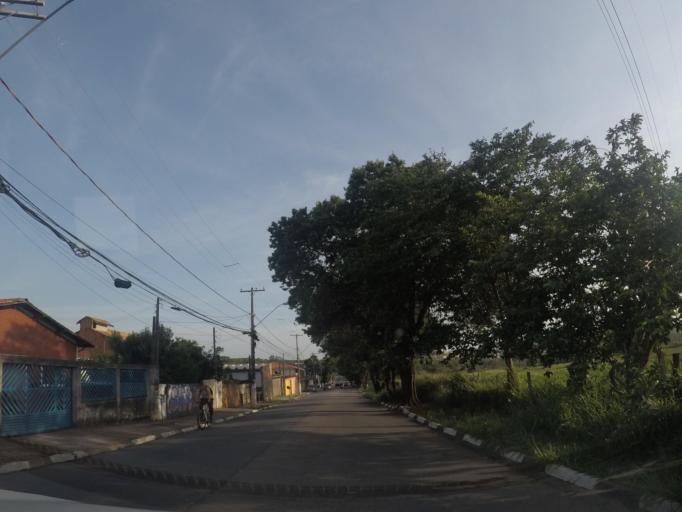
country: BR
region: Sao Paulo
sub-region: Hortolandia
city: Hortolandia
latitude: -22.8431
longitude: -47.1899
